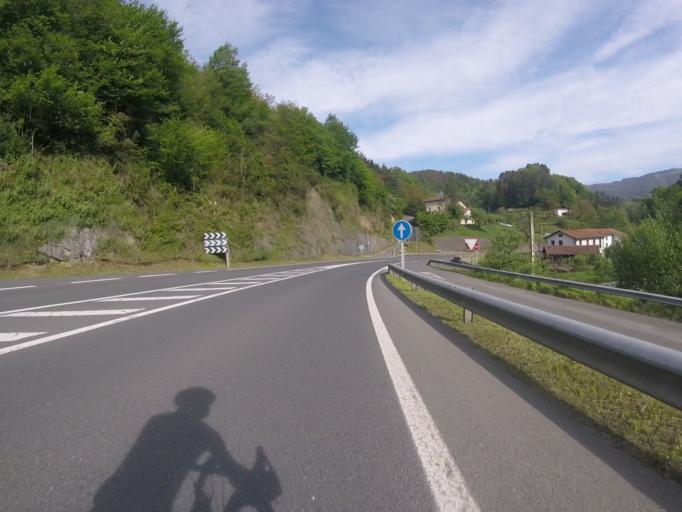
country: ES
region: Basque Country
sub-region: Provincia de Guipuzcoa
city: Urretxu
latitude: 43.0991
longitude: -2.3176
